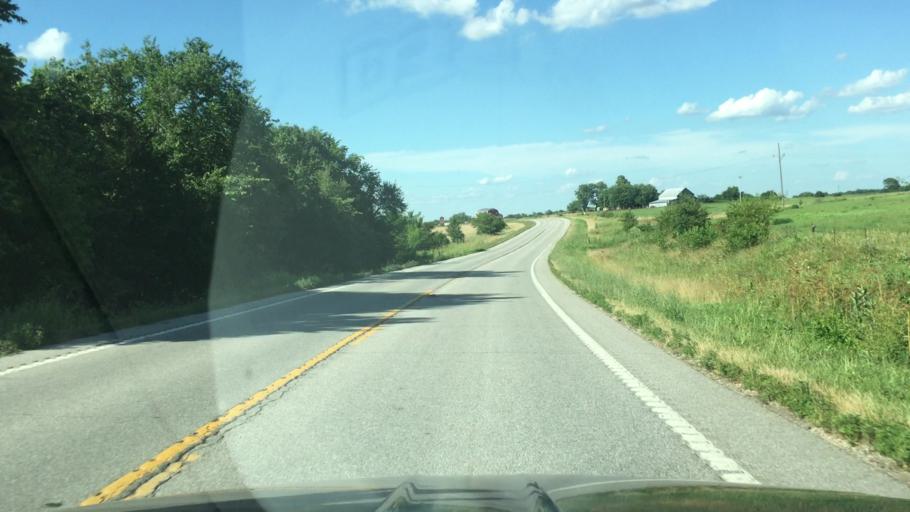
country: US
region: Missouri
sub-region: Morgan County
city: Versailles
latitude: 38.4993
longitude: -92.8069
